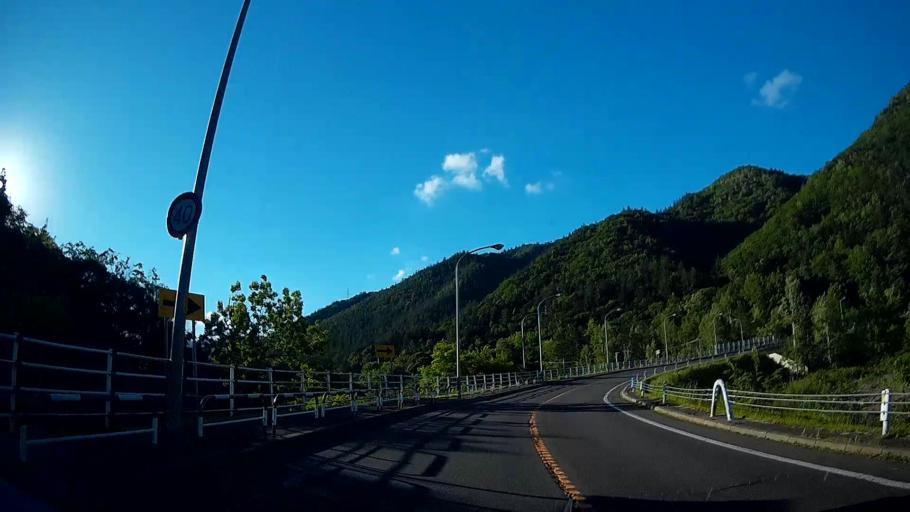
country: JP
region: Hokkaido
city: Sapporo
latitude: 42.9779
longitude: 141.1360
